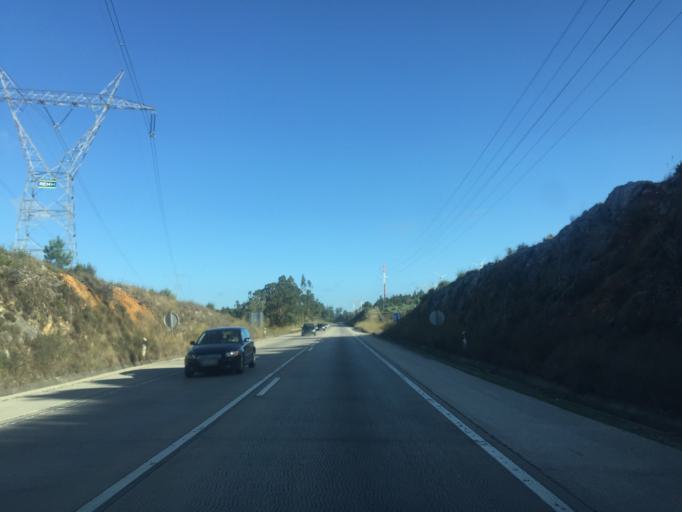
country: PT
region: Santarem
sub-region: Rio Maior
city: Rio Maior
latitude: 39.3538
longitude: -8.9709
